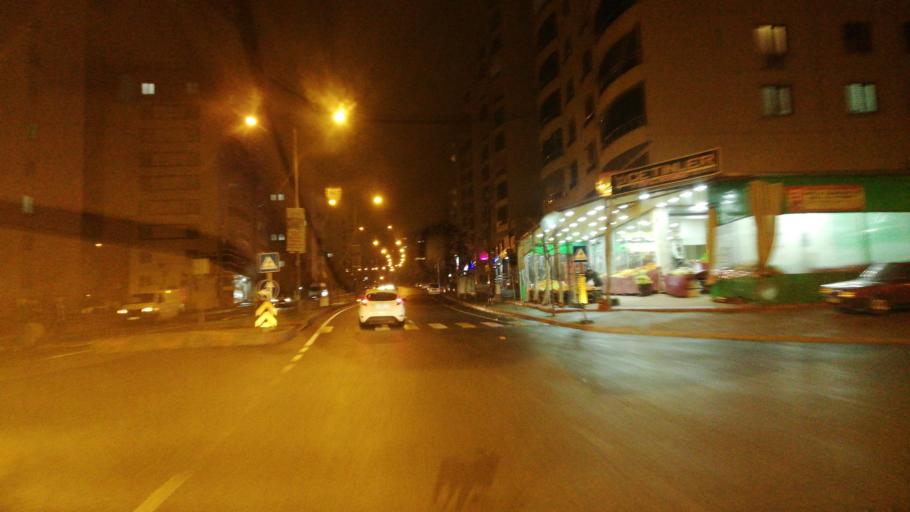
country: TR
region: Kahramanmaras
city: Kahramanmaras
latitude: 37.5867
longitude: 36.8696
